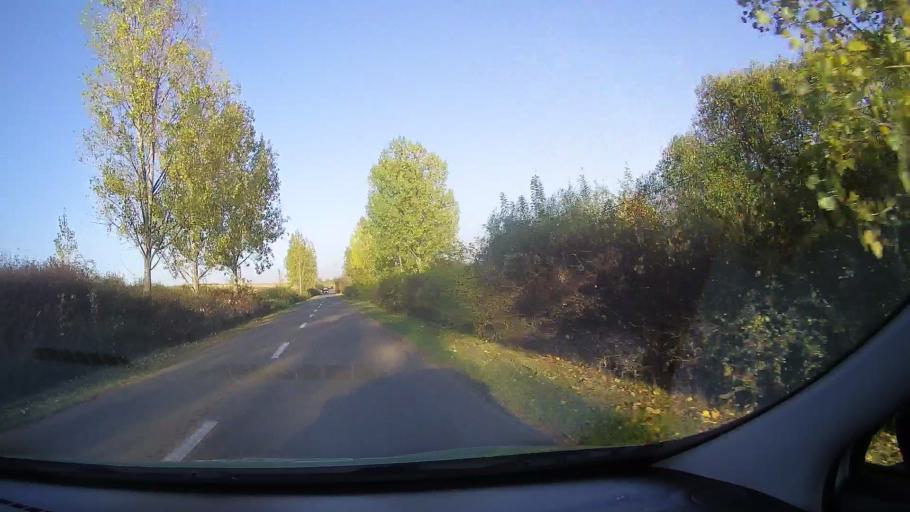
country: RO
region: Bihor
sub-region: Comuna Paleu
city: Paleu
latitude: 47.1261
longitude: 21.9664
